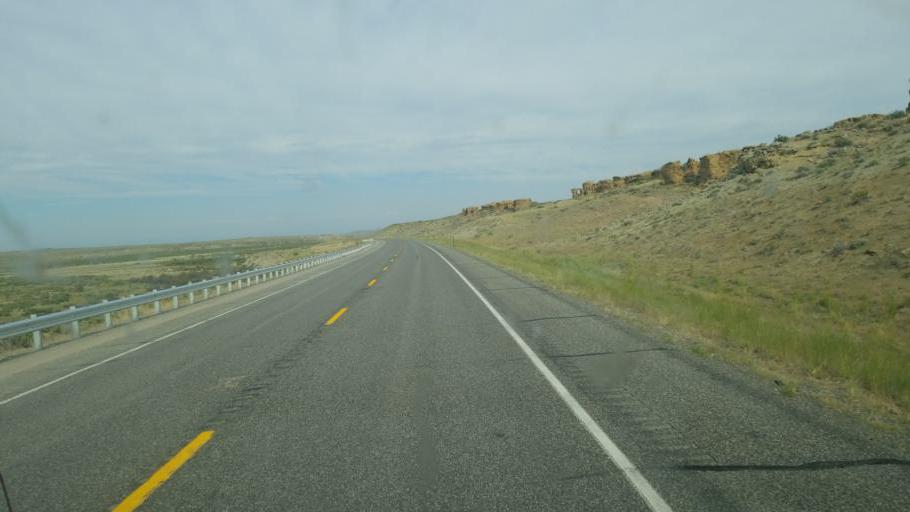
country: US
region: Wyoming
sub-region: Fremont County
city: Riverton
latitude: 43.2230
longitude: -108.0301
